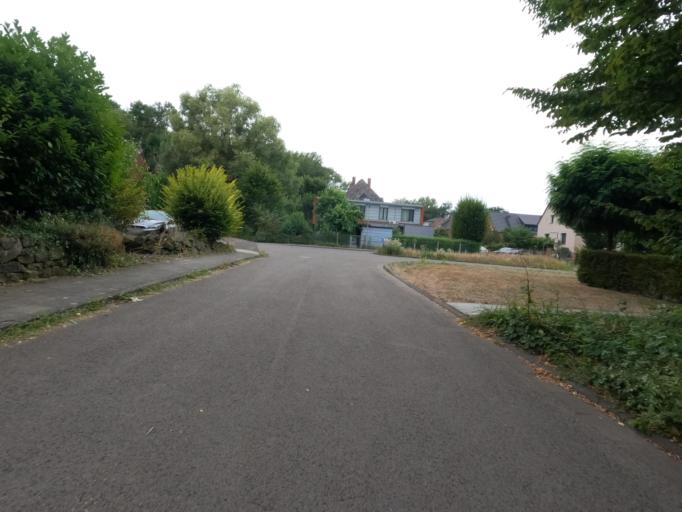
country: DE
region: North Rhine-Westphalia
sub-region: Regierungsbezirk Koln
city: Aldenhoven
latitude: 50.9451
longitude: 6.3094
